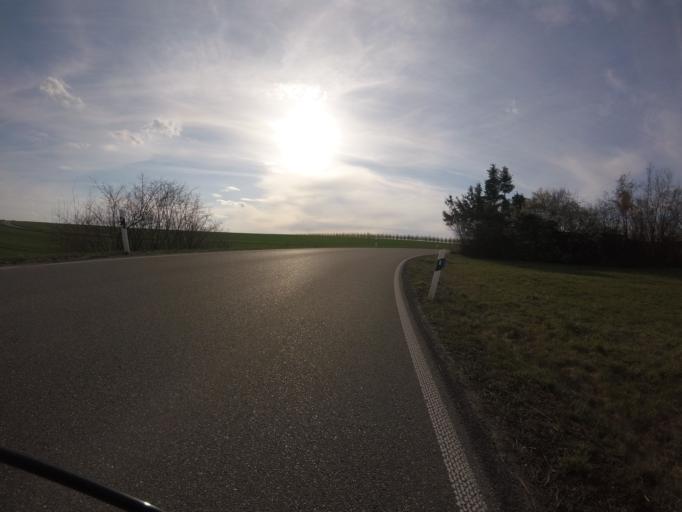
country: DE
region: Baden-Wuerttemberg
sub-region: Regierungsbezirk Stuttgart
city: Kirchberg an der Murr
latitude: 48.9402
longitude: 9.3544
